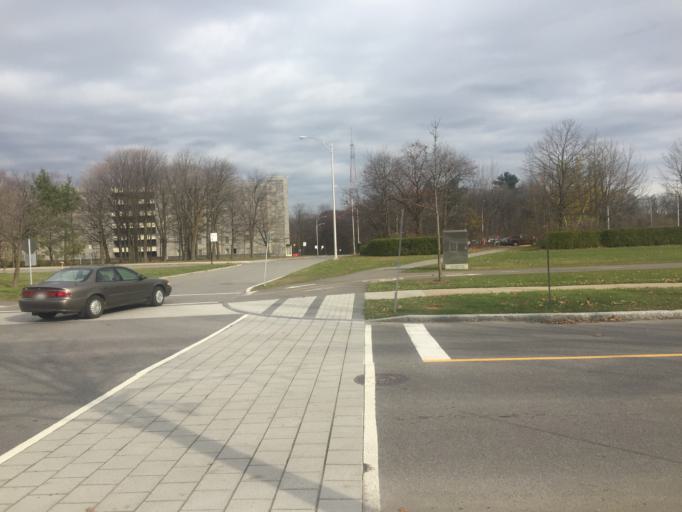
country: CA
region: Quebec
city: Quebec
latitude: 46.7812
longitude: -71.2709
